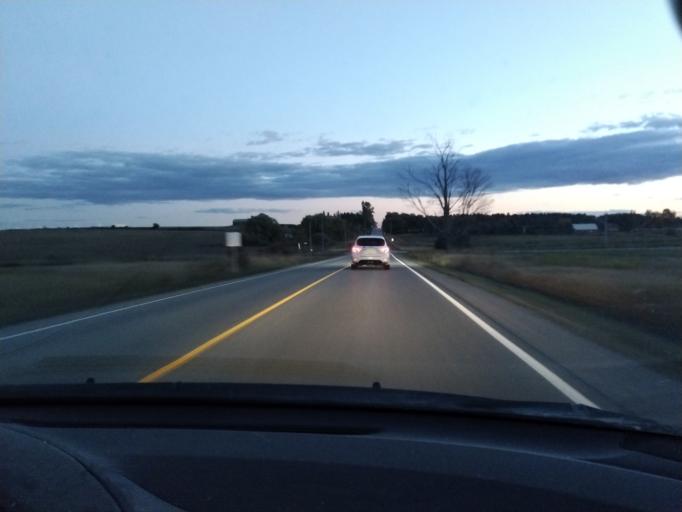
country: CA
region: Ontario
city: Bradford West Gwillimbury
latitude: 44.1357
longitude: -79.6484
